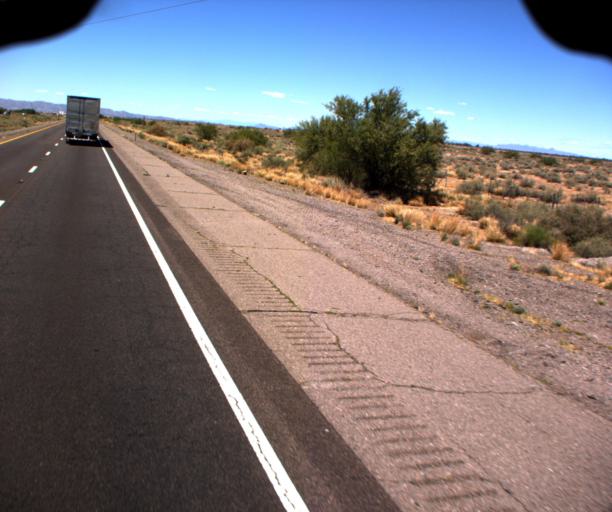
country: US
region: Arizona
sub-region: Maricopa County
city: Sun Lakes
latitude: 33.1668
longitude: -111.8795
